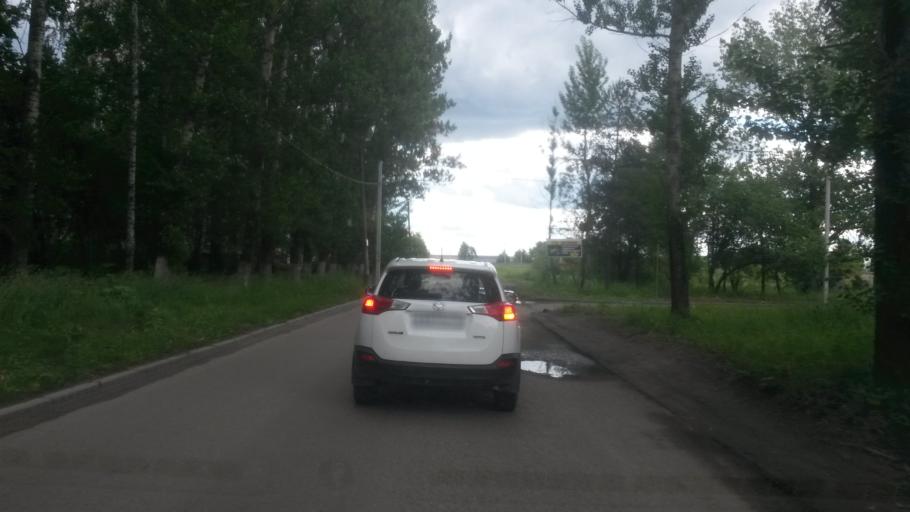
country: RU
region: Jaroslavl
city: Yaroslavl
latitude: 57.6723
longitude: 39.7780
